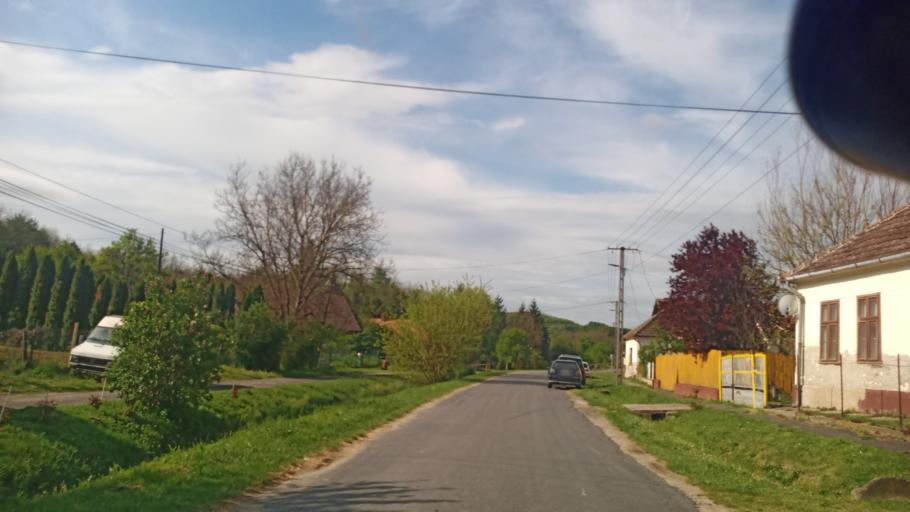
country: HU
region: Zala
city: Pacsa
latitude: 46.6684
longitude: 17.0517
